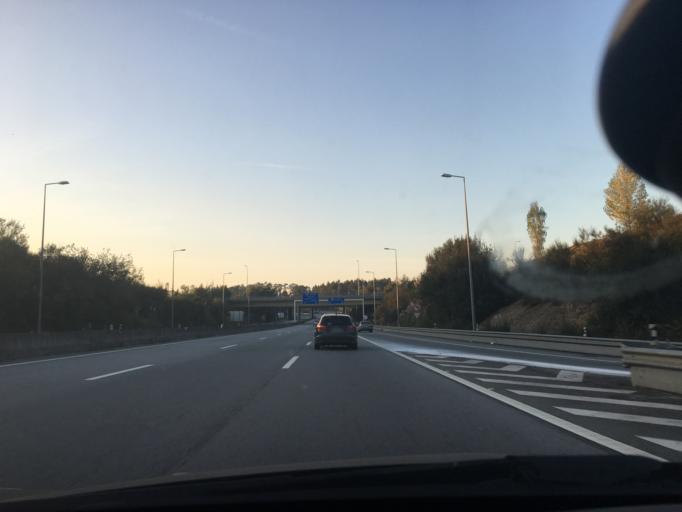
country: PT
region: Porto
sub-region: Matosinhos
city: Santa Cruz do Bispo
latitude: 41.2233
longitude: -8.6621
